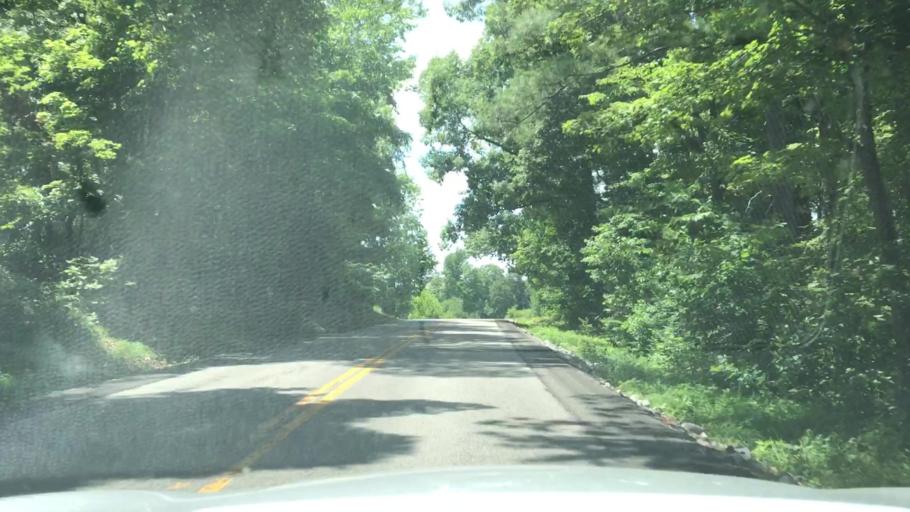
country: US
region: Kentucky
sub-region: Muhlenberg County
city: Greenville
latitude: 37.1245
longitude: -87.3115
